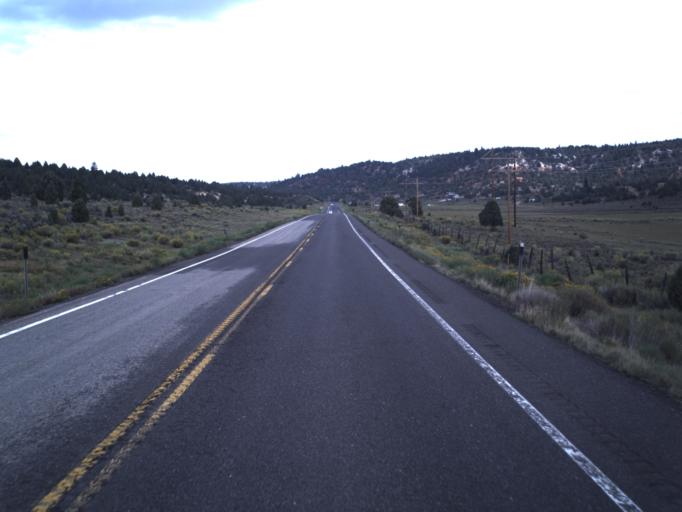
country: US
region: Utah
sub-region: Garfield County
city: Panguitch
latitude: 37.5202
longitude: -112.4948
